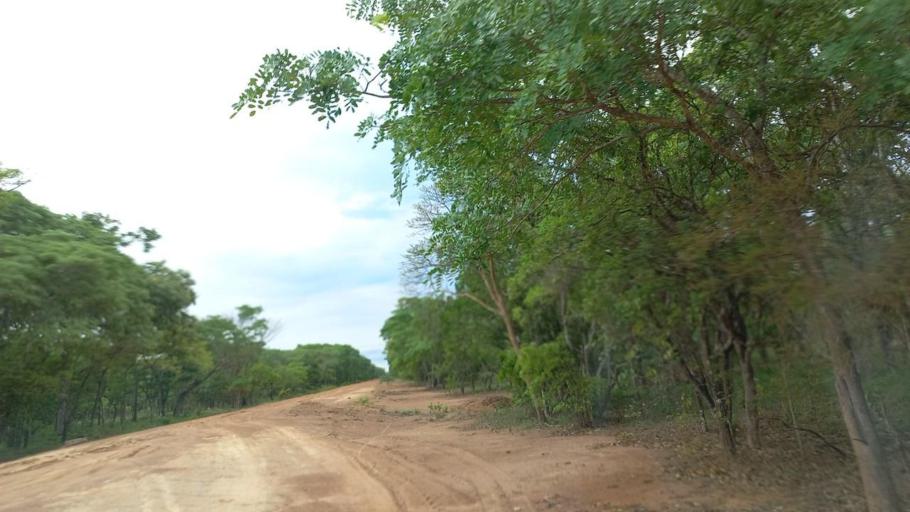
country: ZM
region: North-Western
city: Kalengwa
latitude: -13.3732
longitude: 25.0735
